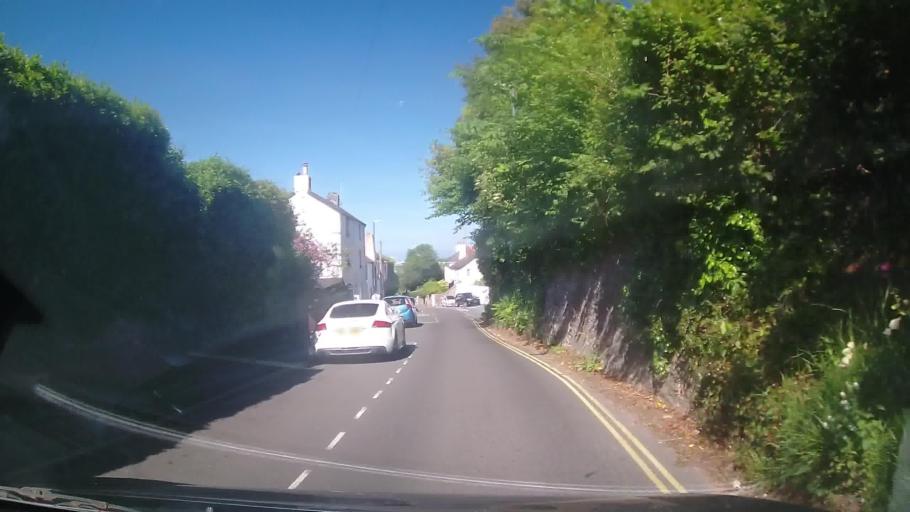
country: GB
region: England
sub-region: Borough of Torbay
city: Brixham
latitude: 50.3817
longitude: -3.5286
